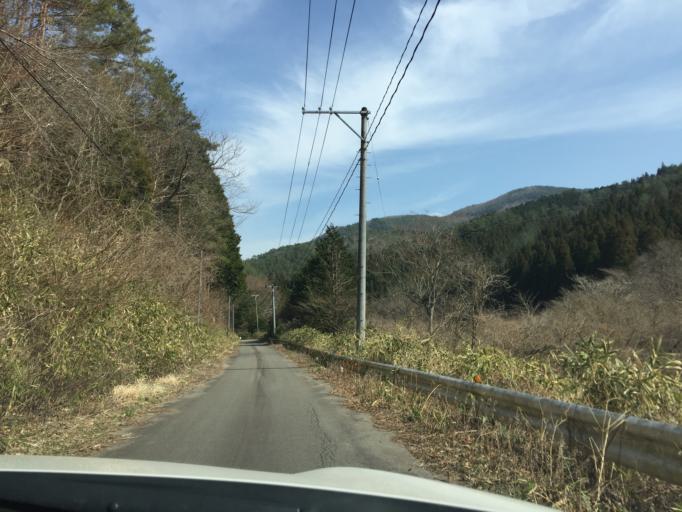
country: JP
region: Fukushima
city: Iwaki
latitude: 37.1275
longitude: 140.7791
